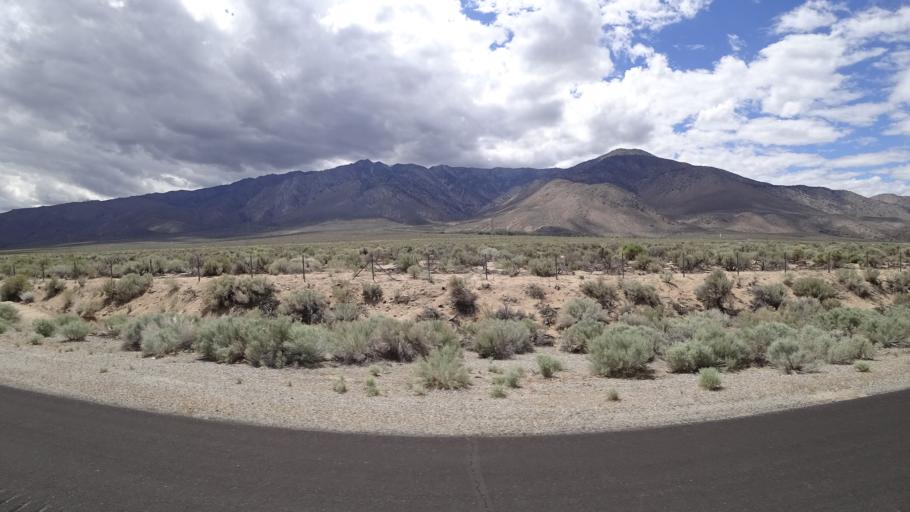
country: US
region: California
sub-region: Inyo County
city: Big Pine
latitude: 37.2546
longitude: -118.3591
